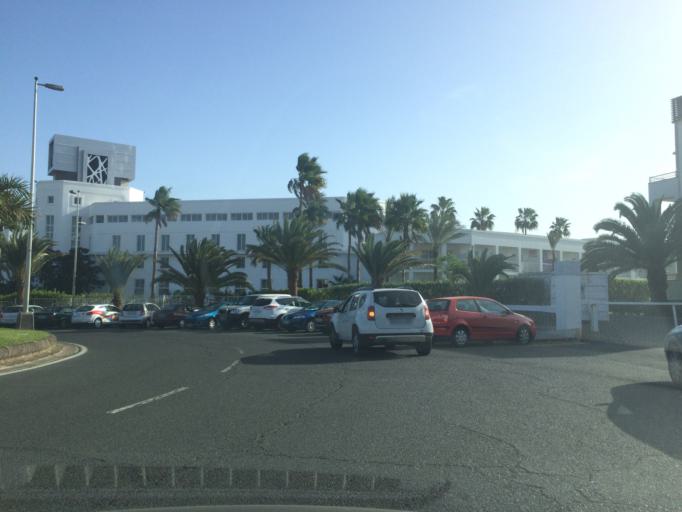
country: ES
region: Canary Islands
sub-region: Provincia de Las Palmas
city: Maspalomas
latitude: 27.7412
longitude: -15.6036
